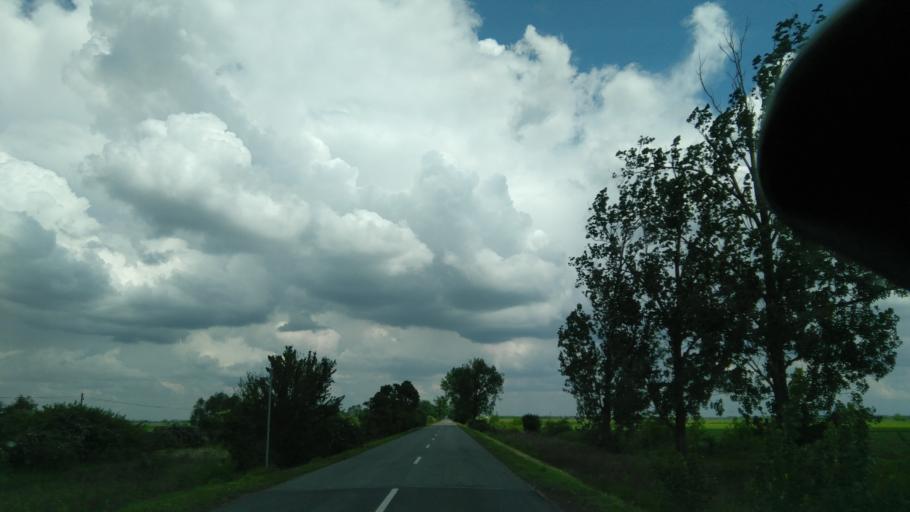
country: HU
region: Bekes
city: Devavanya
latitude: 46.9976
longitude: 20.9085
